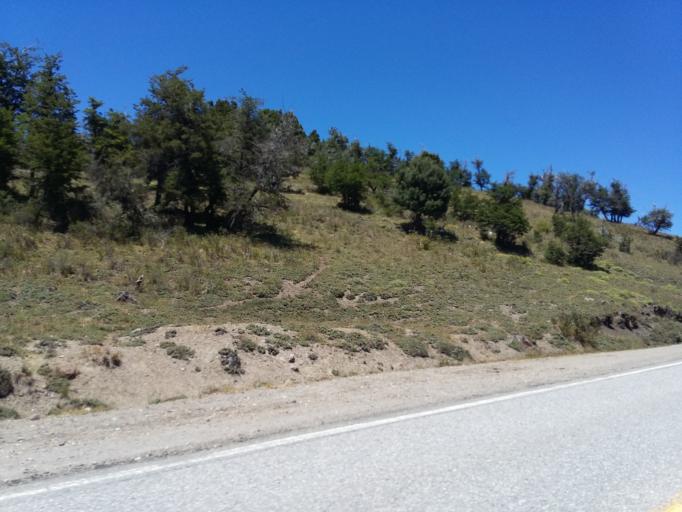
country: AR
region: Neuquen
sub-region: Departamento de Lacar
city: San Martin de los Andes
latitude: -40.1972
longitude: -71.3594
